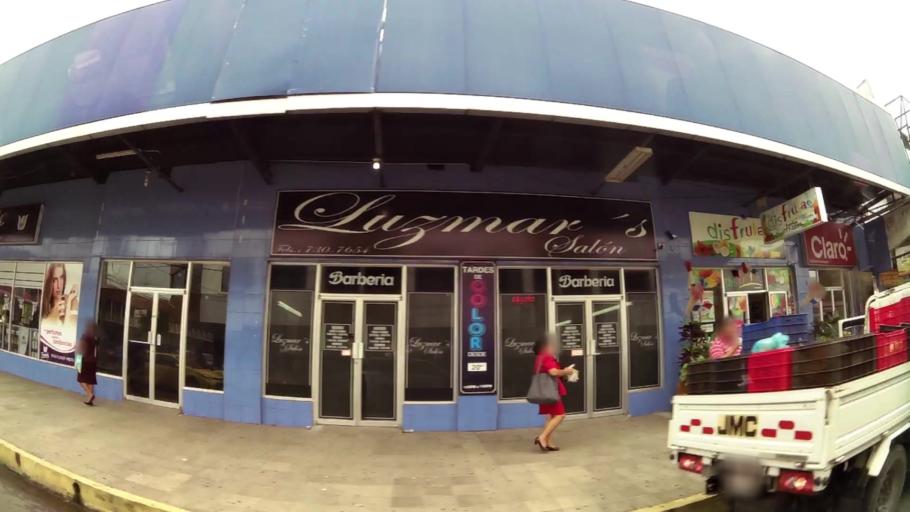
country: PA
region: Chiriqui
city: David
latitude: 8.4278
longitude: -82.4262
